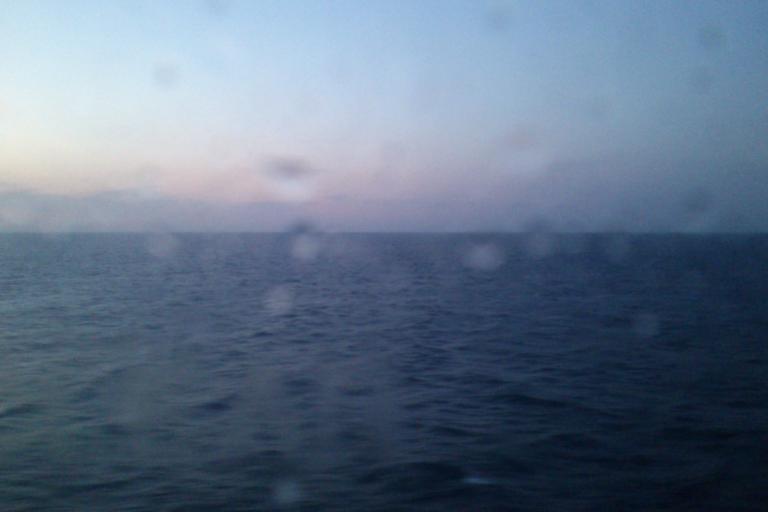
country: JP
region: Ishikawa
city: Kanazawa-shi
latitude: 37.0777
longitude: 136.0116
